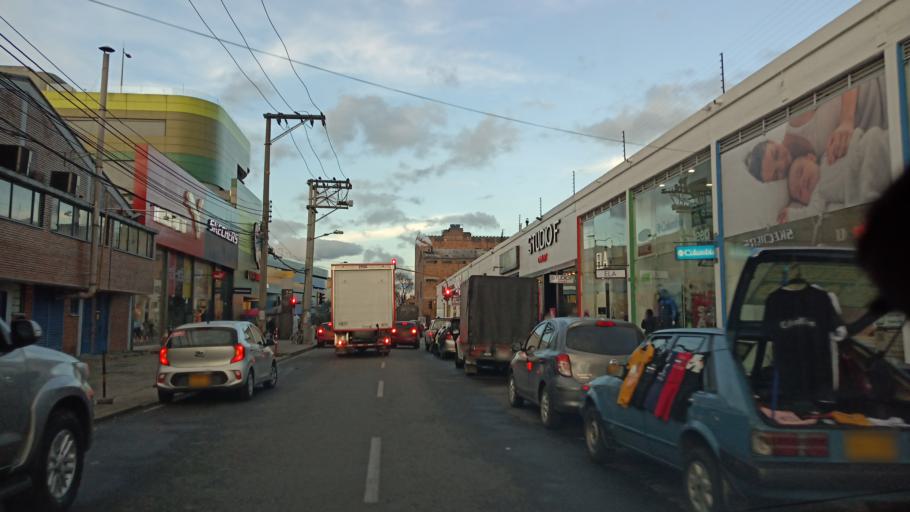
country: CO
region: Bogota D.C.
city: Bogota
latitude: 4.6300
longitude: -74.1161
